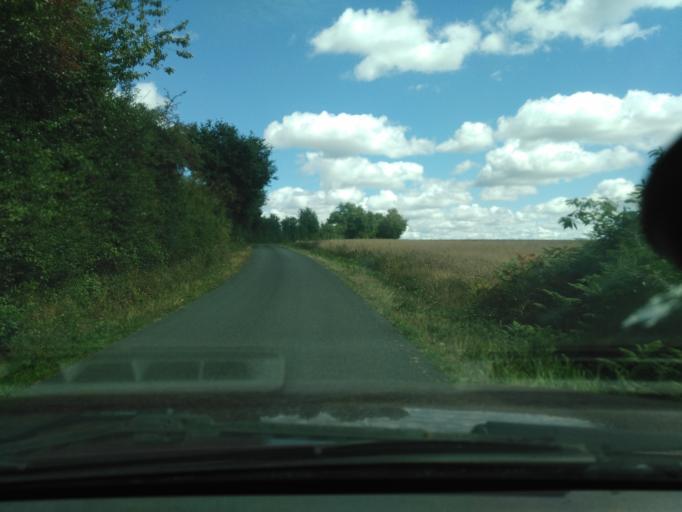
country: FR
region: Pays de la Loire
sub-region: Departement de la Vendee
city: Dompierre-sur-Yon
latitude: 46.7403
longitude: -1.3739
